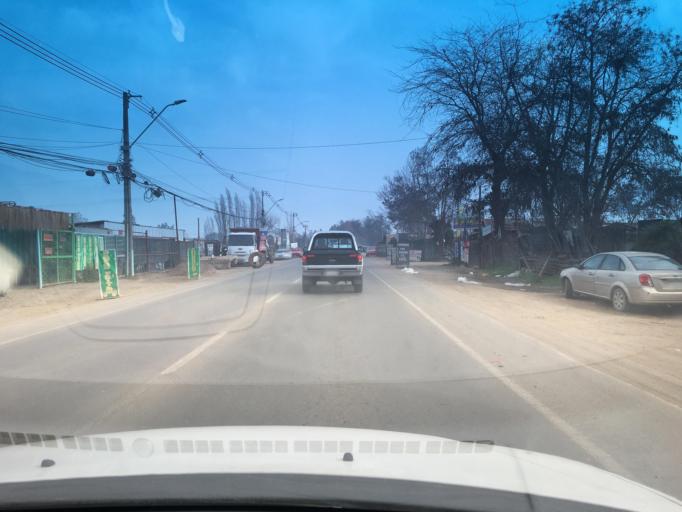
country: CL
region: Santiago Metropolitan
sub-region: Provincia de Chacabuco
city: Lampa
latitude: -33.3083
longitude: -70.8465
